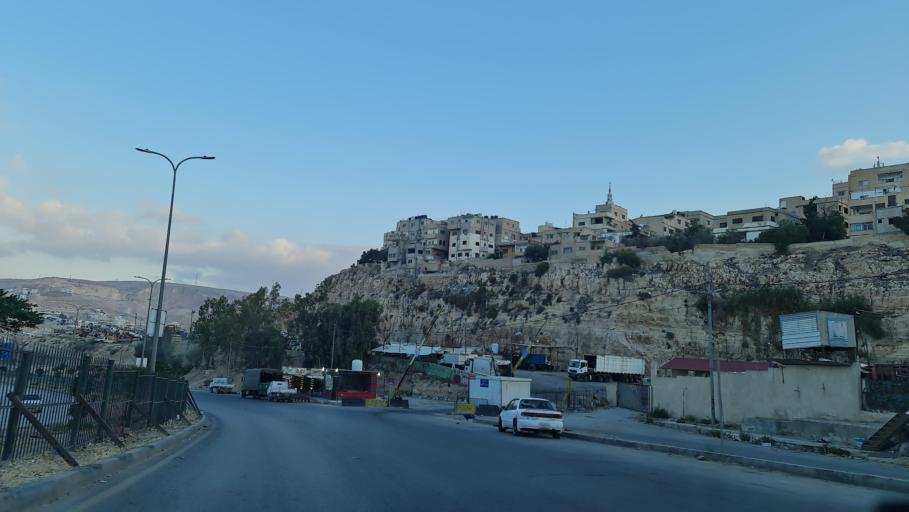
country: JO
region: Zarqa
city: Zarqa
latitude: 32.0794
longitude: 36.0732
